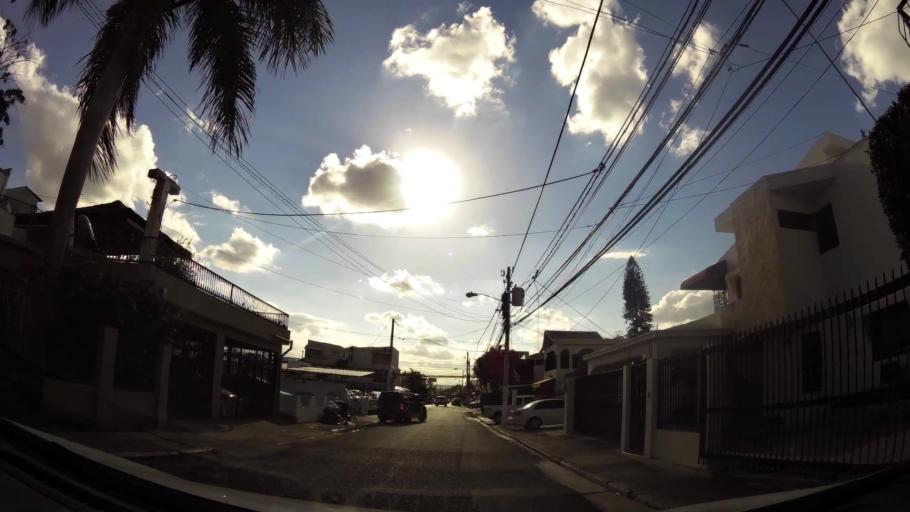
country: DO
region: Santiago
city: Santiago de los Caballeros
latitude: 19.4616
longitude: -70.6914
